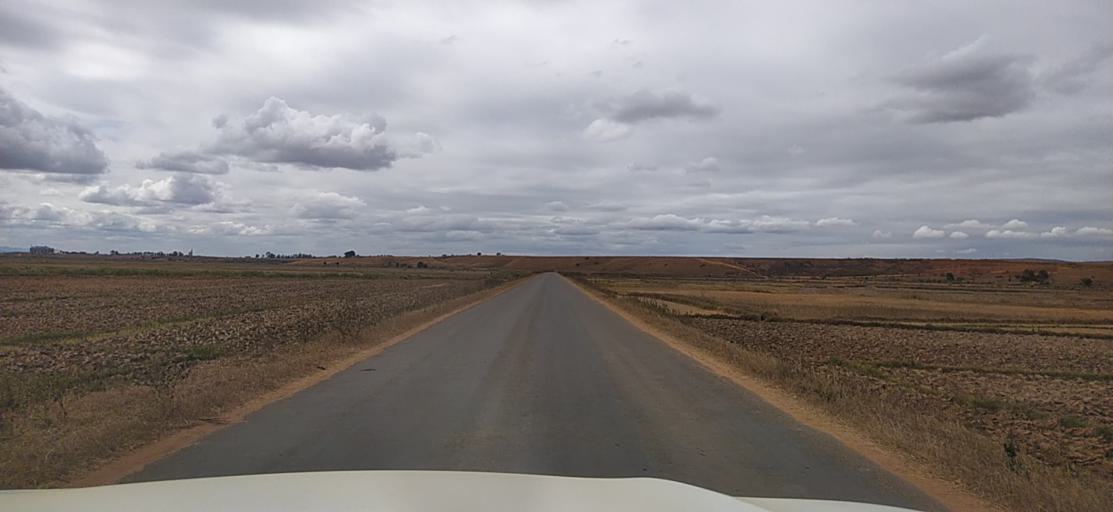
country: MG
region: Alaotra Mangoro
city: Ambatondrazaka
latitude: -17.9194
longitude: 48.2579
